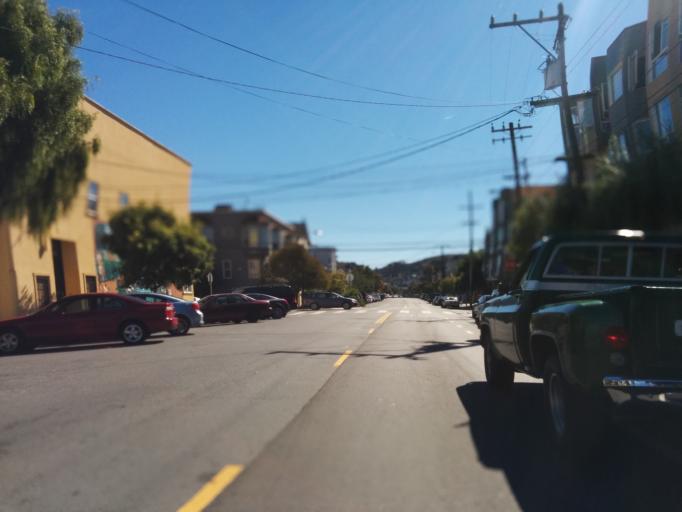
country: US
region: California
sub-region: San Francisco County
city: San Francisco
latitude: 37.7547
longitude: -122.4121
